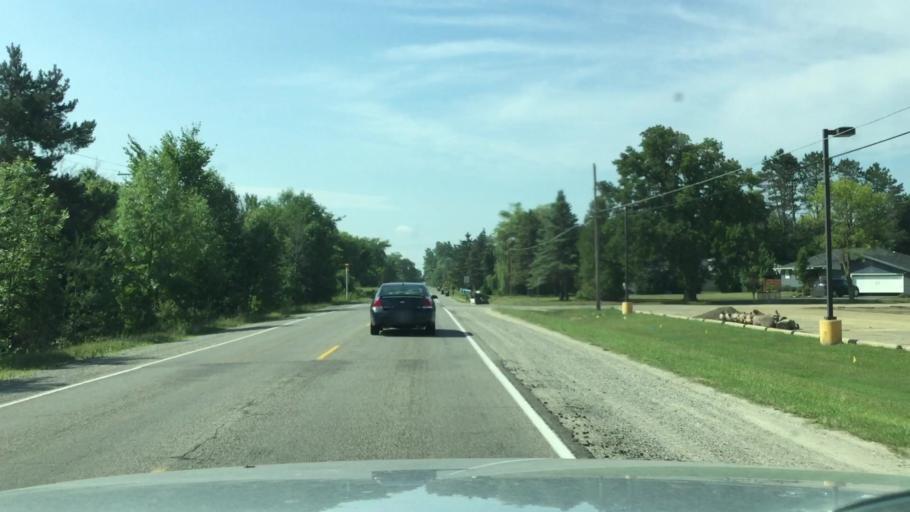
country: US
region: Michigan
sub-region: Genesee County
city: Flushing
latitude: 43.0935
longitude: -83.8136
